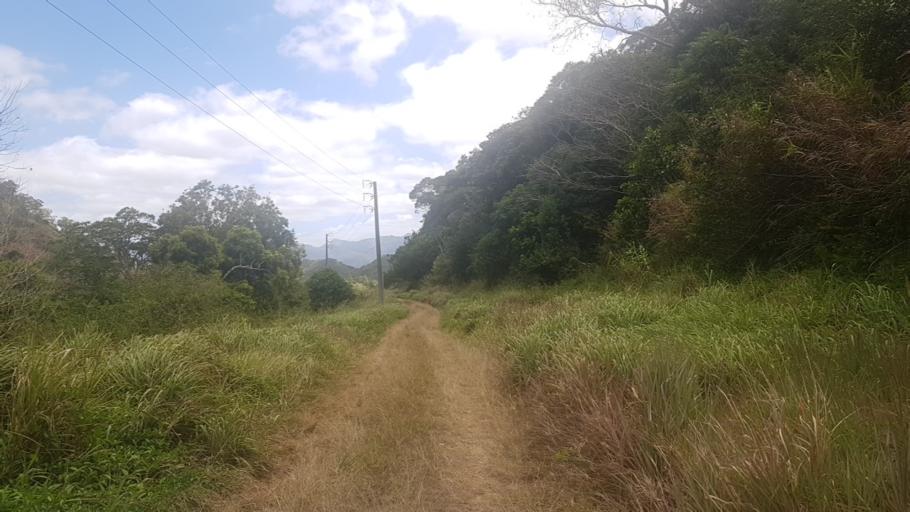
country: NC
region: South Province
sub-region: Dumbea
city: Dumbea
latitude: -22.1869
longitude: 166.4797
